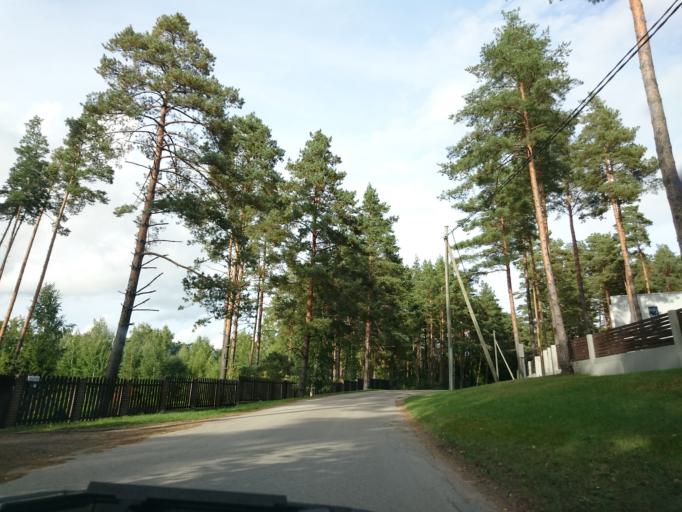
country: LV
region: Adazi
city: Adazi
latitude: 57.0406
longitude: 24.3331
